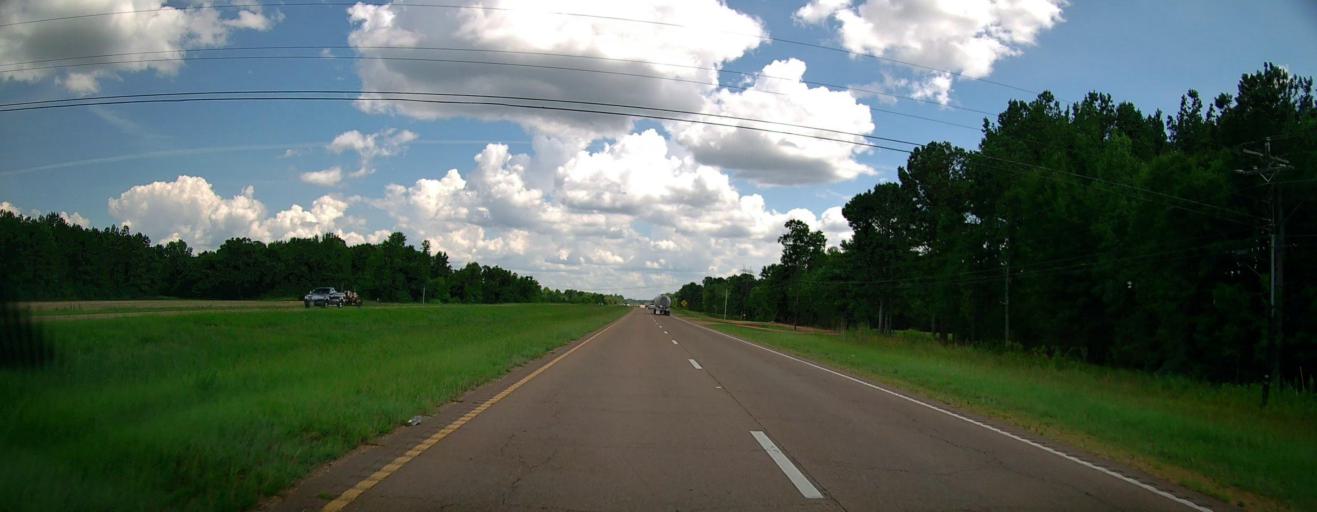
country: US
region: Mississippi
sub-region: Lowndes County
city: Columbus Air Force Base
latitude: 33.6839
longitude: -88.4350
